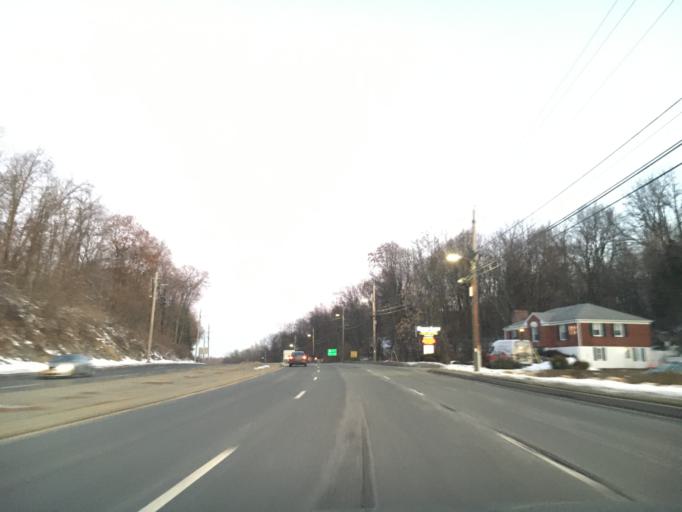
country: US
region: New York
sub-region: Dutchess County
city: Crown Heights
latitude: 41.6311
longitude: -73.9160
